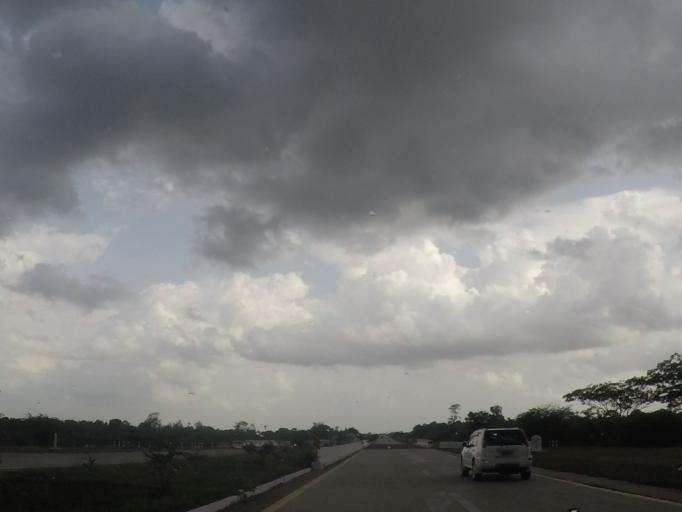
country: MM
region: Mandalay
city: Meiktila
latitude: 20.8598
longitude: 95.7691
